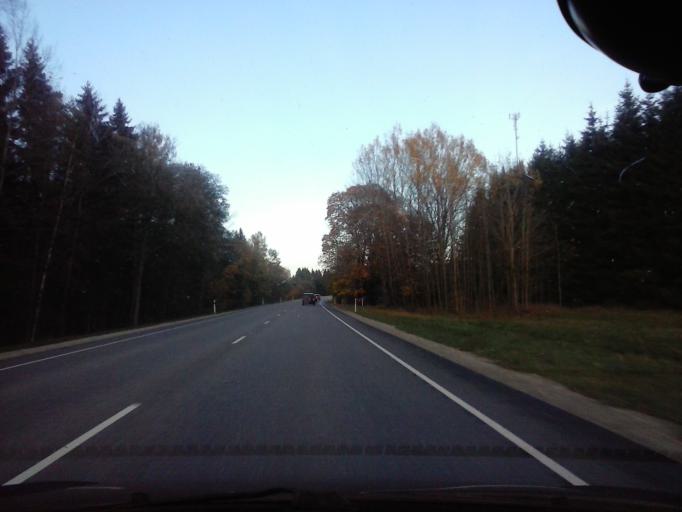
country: EE
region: Harju
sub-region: Nissi vald
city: Turba
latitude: 58.9895
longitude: 24.0199
